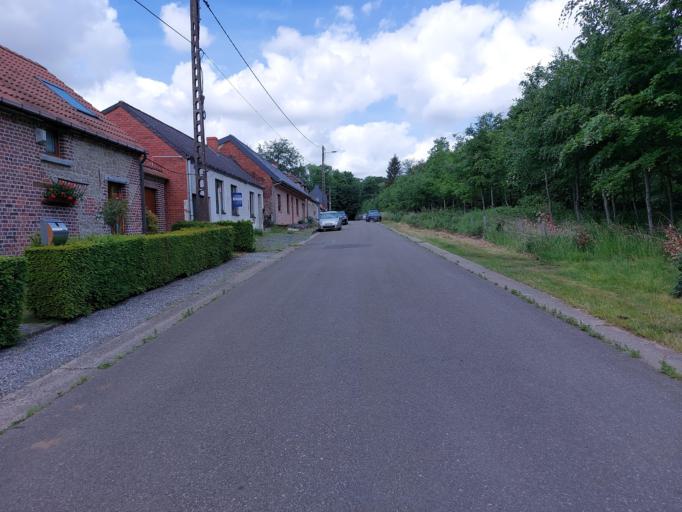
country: BE
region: Wallonia
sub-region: Province du Hainaut
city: Saint-Ghislain
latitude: 50.4902
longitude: 3.8362
